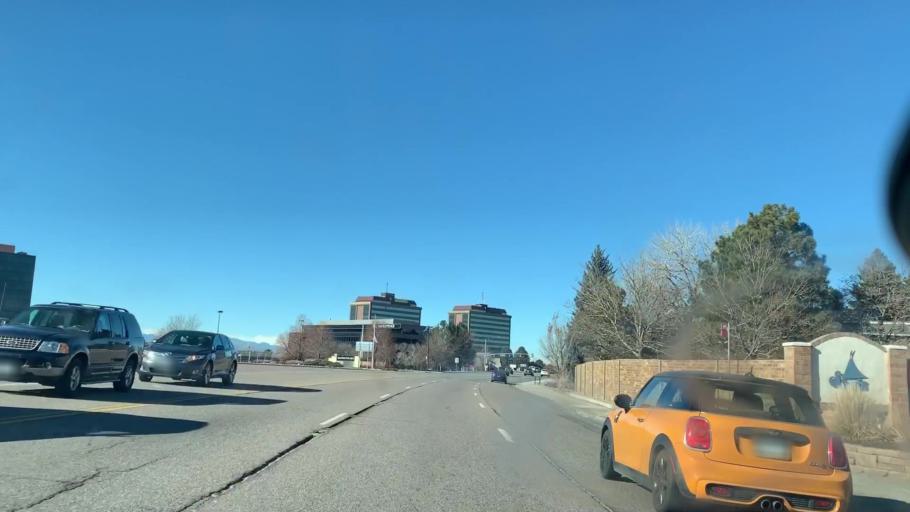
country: US
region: Colorado
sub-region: Adams County
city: Aurora
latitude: 39.6612
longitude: -104.8559
